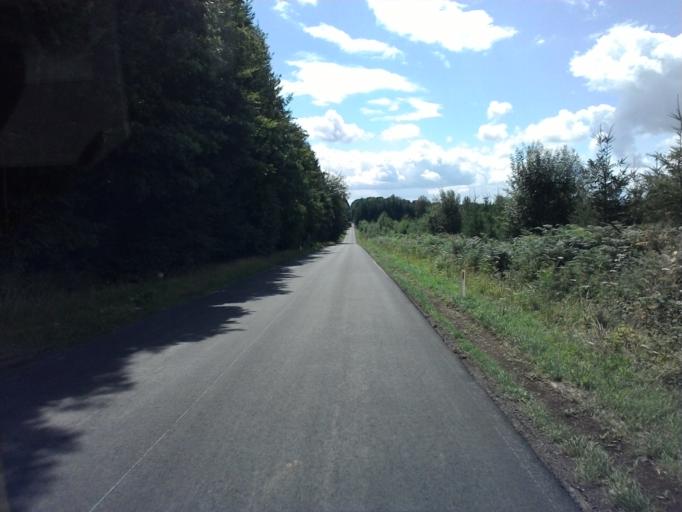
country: BE
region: Wallonia
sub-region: Province du Luxembourg
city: Habay-la-Vieille
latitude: 49.7595
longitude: 5.6232
